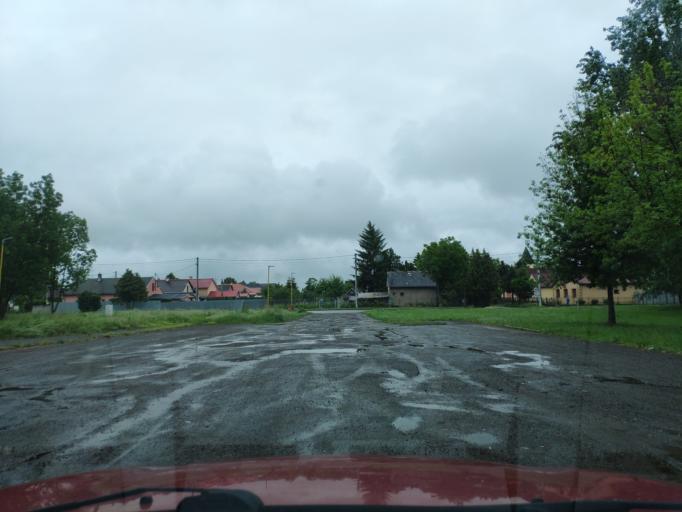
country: SK
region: Kosicky
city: Cierna nad Tisou
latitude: 48.4186
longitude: 22.0903
